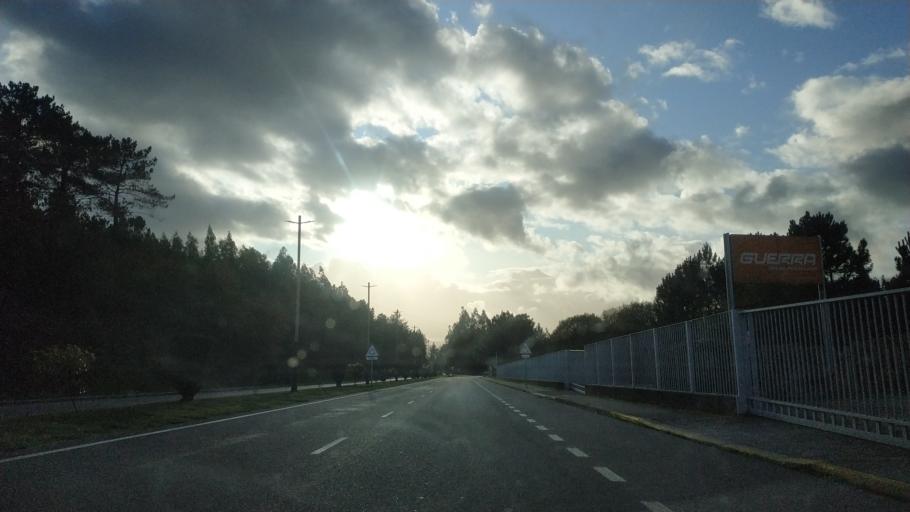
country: ES
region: Galicia
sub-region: Provincia de Pontevedra
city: Silleda
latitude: 42.7899
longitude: -8.1629
